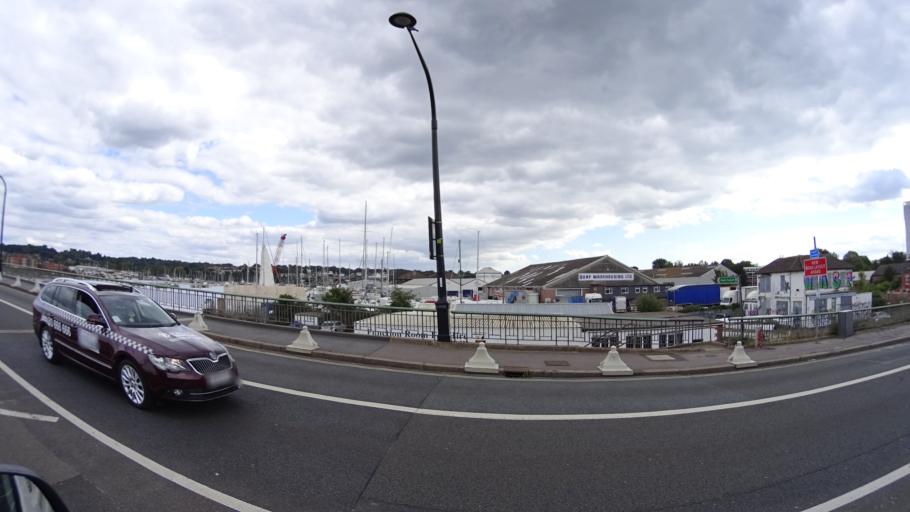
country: GB
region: England
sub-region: Southampton
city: Southampton
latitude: 50.9135
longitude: -1.3872
